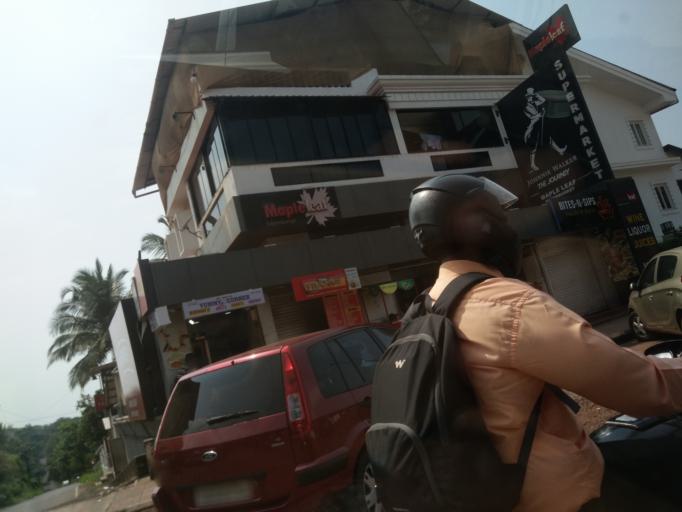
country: IN
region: Goa
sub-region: North Goa
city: Serula
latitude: 15.5356
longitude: 73.8205
